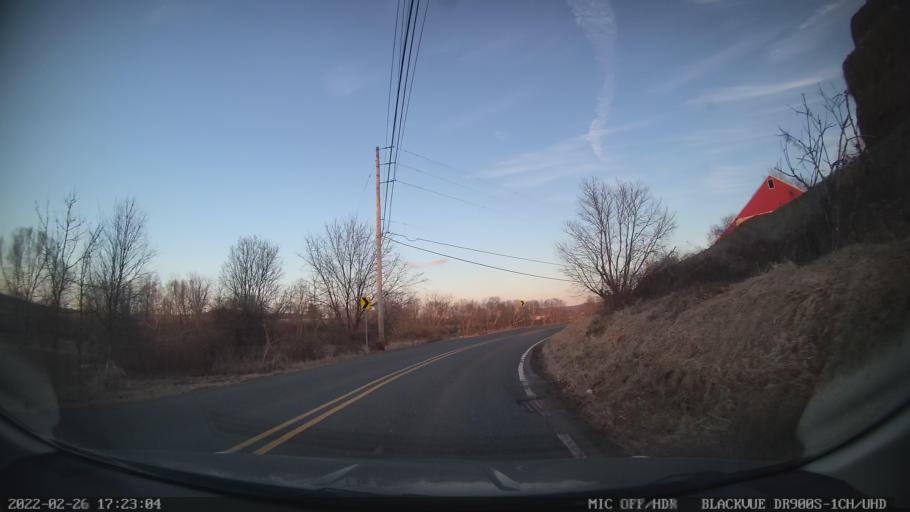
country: US
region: Pennsylvania
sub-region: Berks County
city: Bally
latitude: 40.4270
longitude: -75.5601
